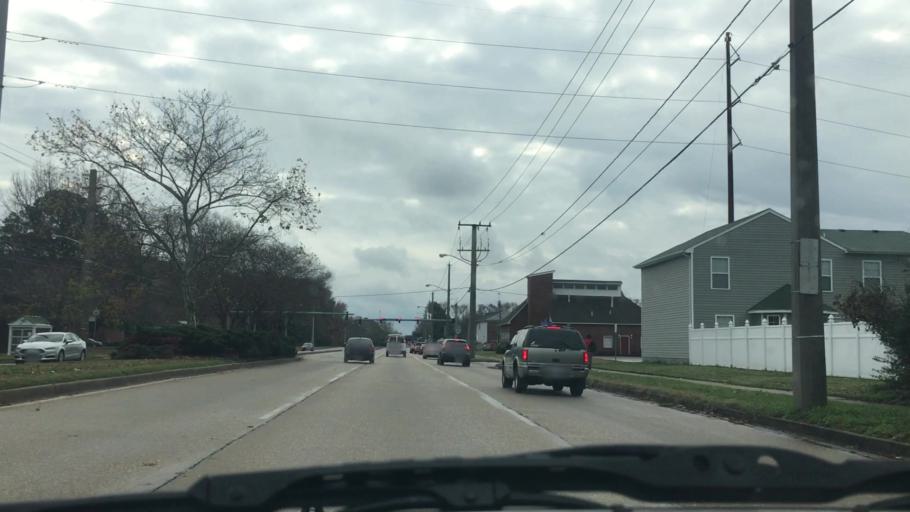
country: US
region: Virginia
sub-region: City of Norfolk
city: Norfolk
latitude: 36.9091
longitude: -76.2407
